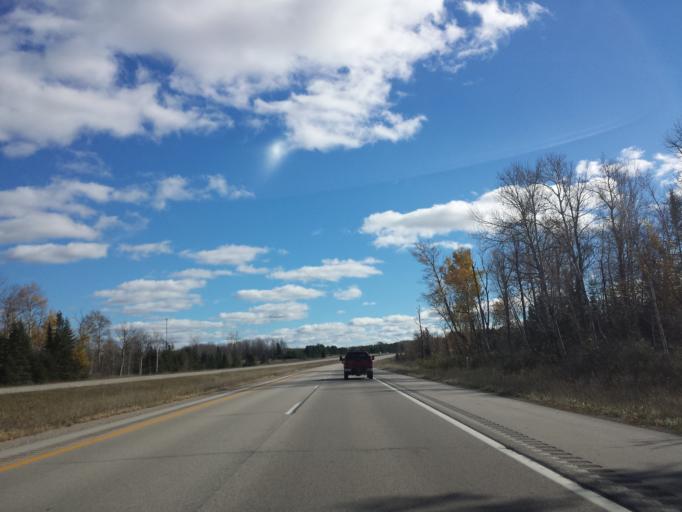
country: US
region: Michigan
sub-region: Cheboygan County
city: Cheboygan
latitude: 45.6154
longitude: -84.6267
